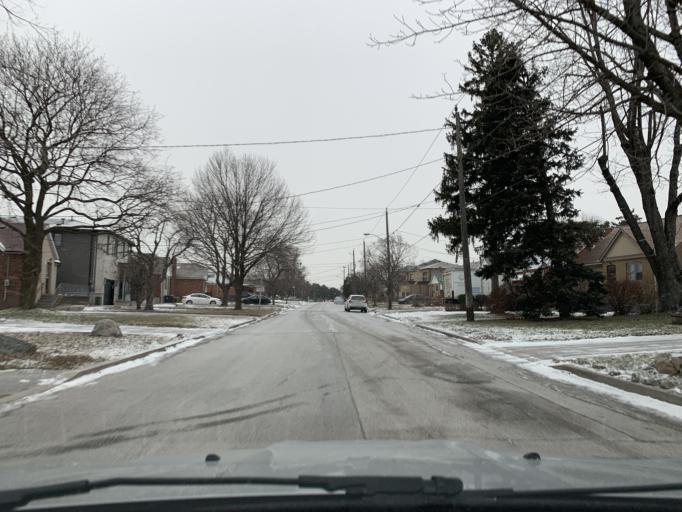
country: CA
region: Ontario
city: Toronto
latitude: 43.7264
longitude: -79.4766
